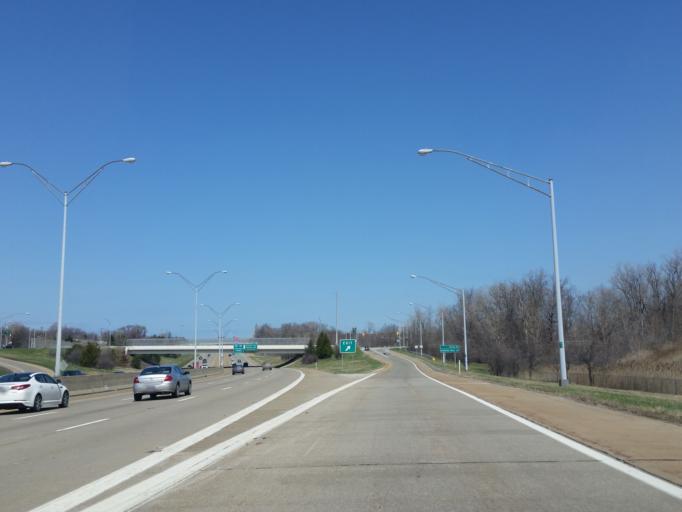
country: US
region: Ohio
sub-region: Cuyahoga County
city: Brooklyn Heights
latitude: 41.4313
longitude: -81.6815
